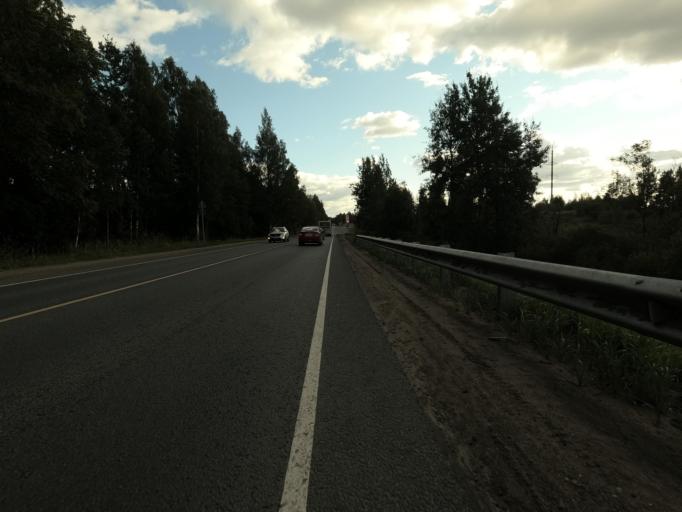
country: RU
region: Leningrad
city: Vsevolozhsk
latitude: 59.9791
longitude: 30.6539
